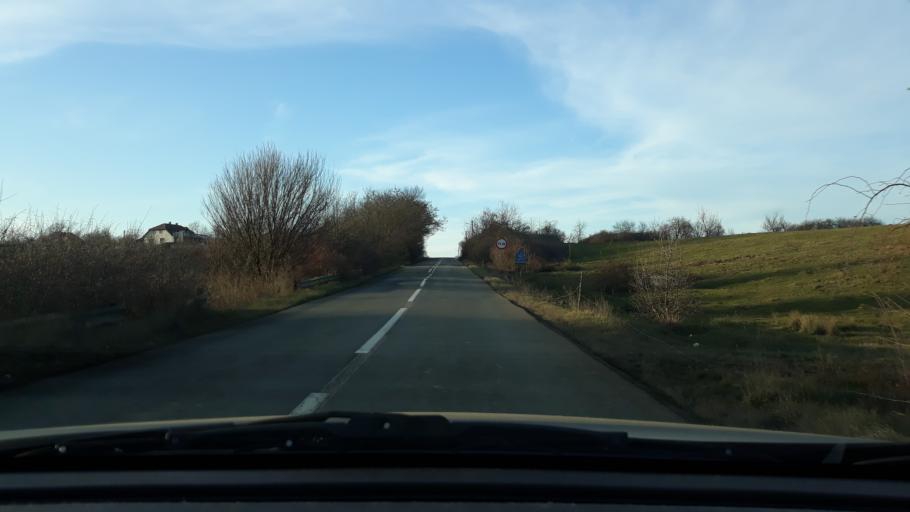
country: RO
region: Bihor
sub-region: Comuna Suplacu de Barcau
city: Suplacu de Barcau
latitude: 47.2717
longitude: 22.4924
